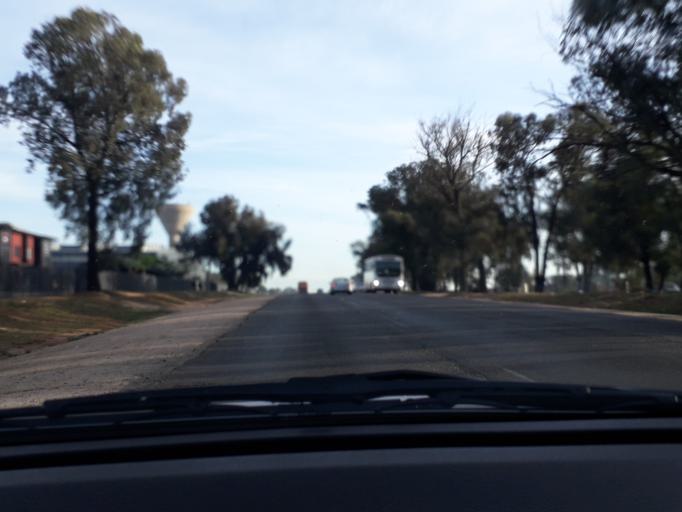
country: ZA
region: Gauteng
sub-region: City of Johannesburg Metropolitan Municipality
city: Midrand
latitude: -25.9415
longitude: 28.1447
